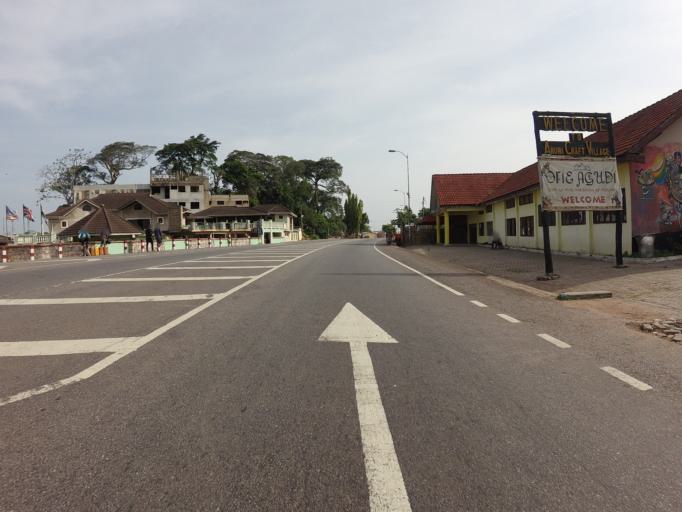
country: GH
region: Eastern
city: Aburi
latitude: 5.8406
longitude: -0.1754
